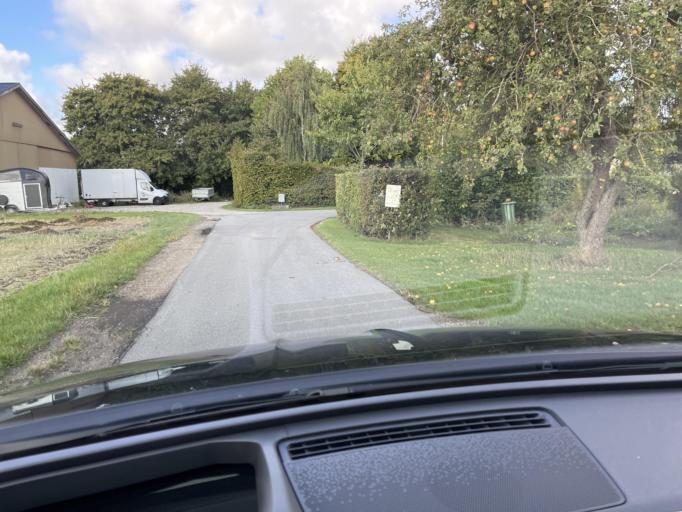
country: DK
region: Zealand
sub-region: Solrod Kommune
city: Havdrup
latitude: 55.5642
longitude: 12.1118
